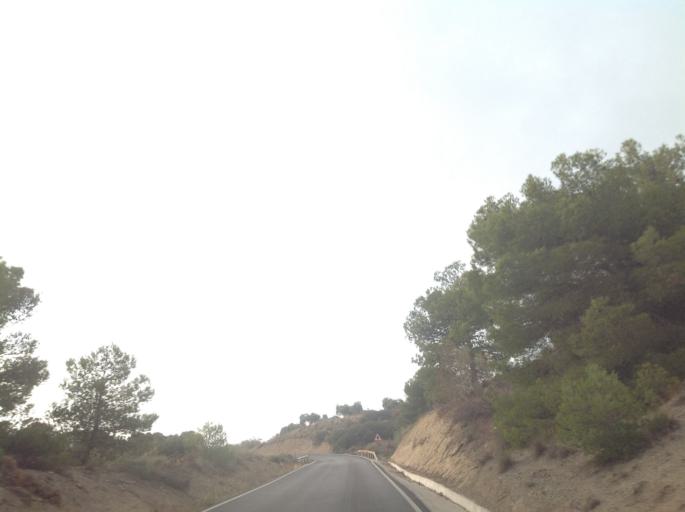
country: ES
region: Andalusia
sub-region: Provincia de Malaga
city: Ardales
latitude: 36.9134
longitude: -4.8050
